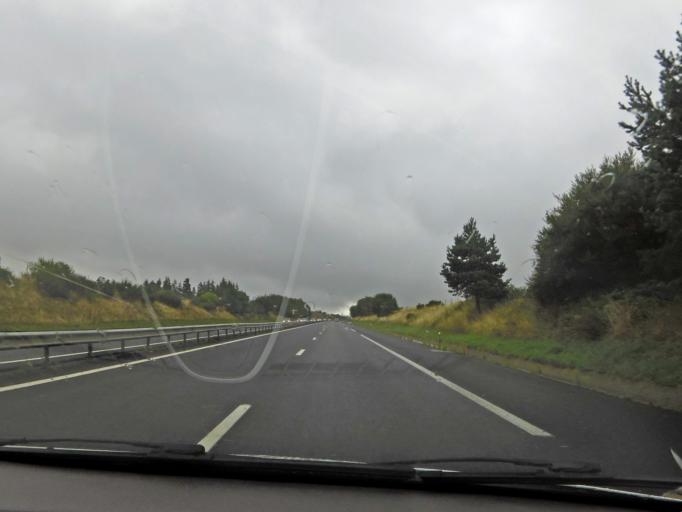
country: FR
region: Auvergne
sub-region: Departement du Cantal
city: Saint-Flour
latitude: 44.9458
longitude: 3.1989
